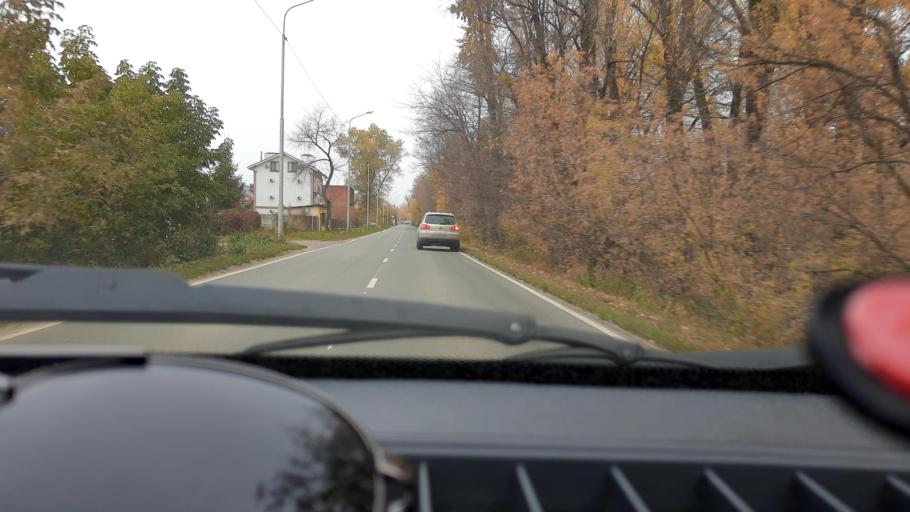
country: RU
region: Bashkortostan
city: Ufa
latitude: 54.6637
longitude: 55.9380
